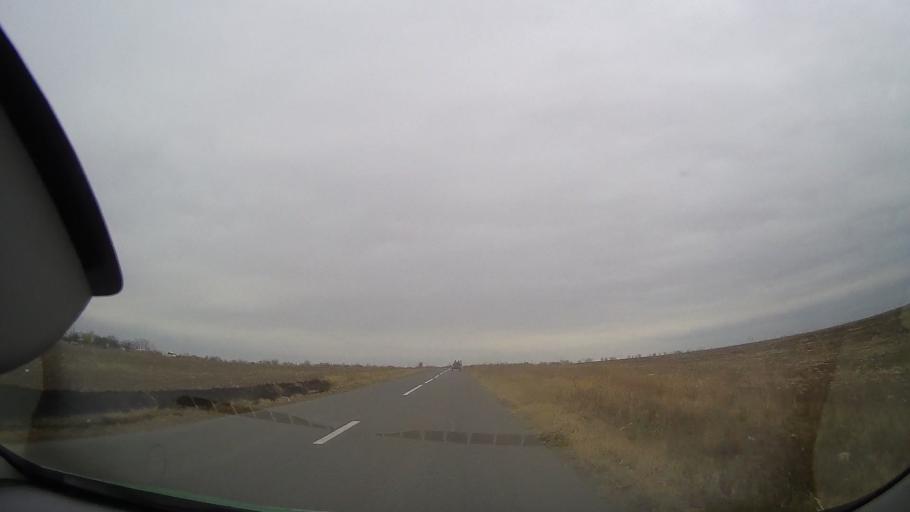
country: RO
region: Braila
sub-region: Comuna Budesti
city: Tataru
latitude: 44.8407
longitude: 27.4239
